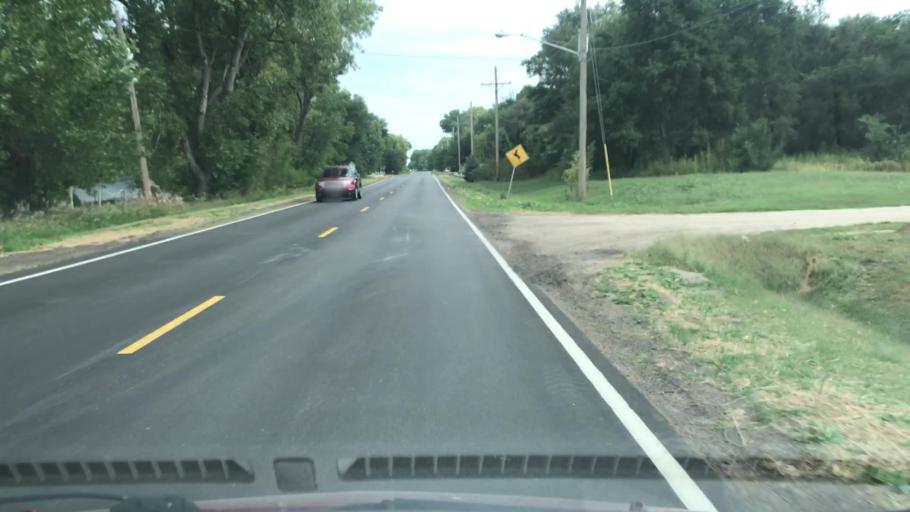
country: US
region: Nebraska
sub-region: Hall County
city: Grand Island
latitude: 40.9194
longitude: -98.3017
